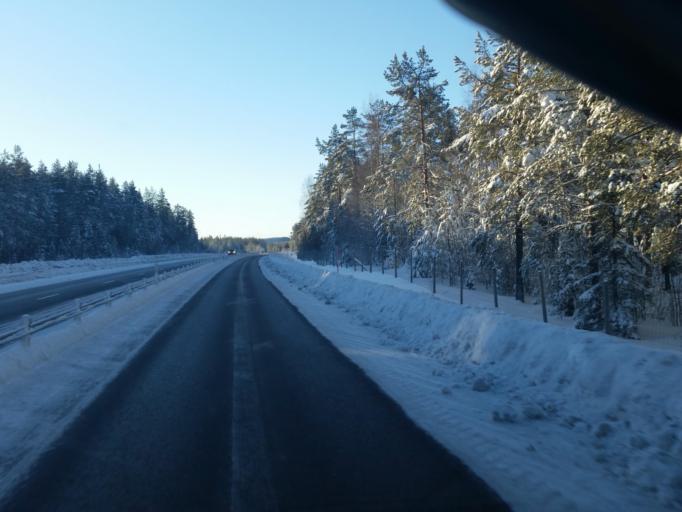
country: SE
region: Norrbotten
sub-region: Pitea Kommun
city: Pitea
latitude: 65.1755
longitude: 21.5018
